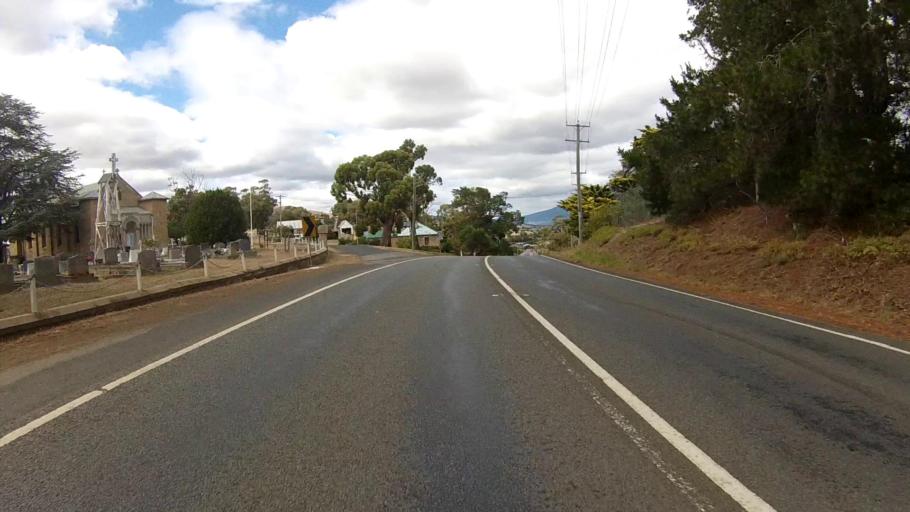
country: AU
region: Tasmania
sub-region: Brighton
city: Bridgewater
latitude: -42.6800
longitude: 147.2658
